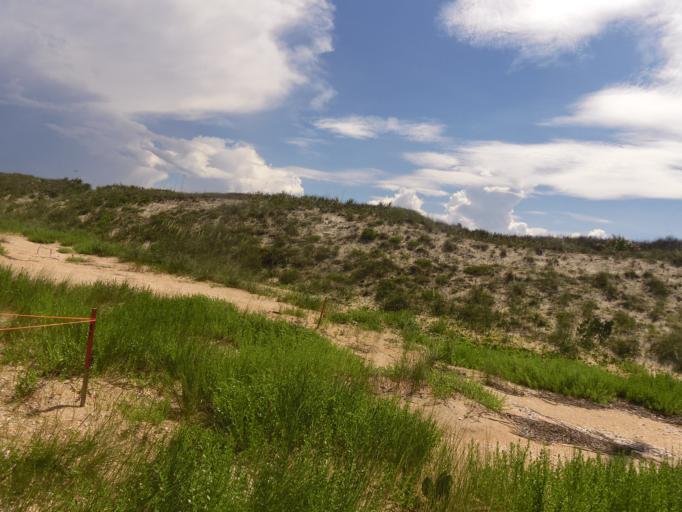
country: US
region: Florida
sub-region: Saint Johns County
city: Palm Valley
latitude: 30.1032
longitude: -81.3416
